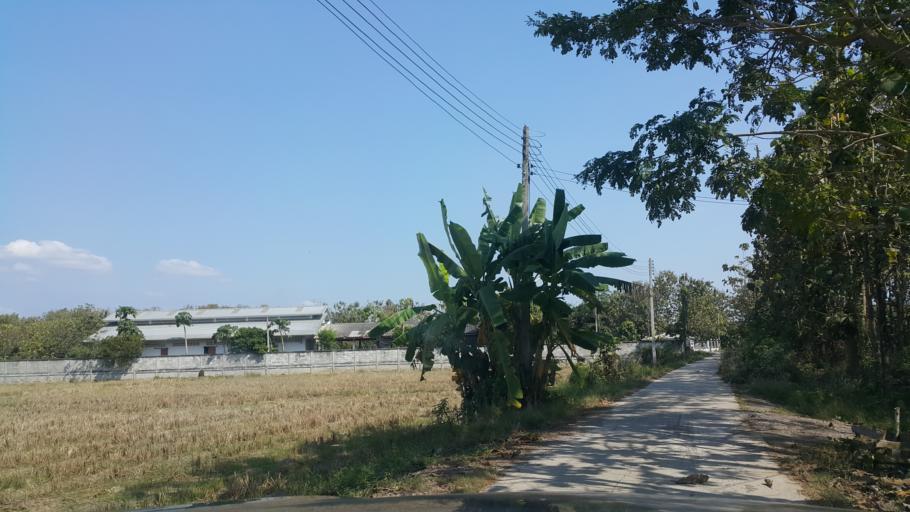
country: TH
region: Sukhothai
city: Thung Saliam
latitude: 17.3196
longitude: 99.5765
